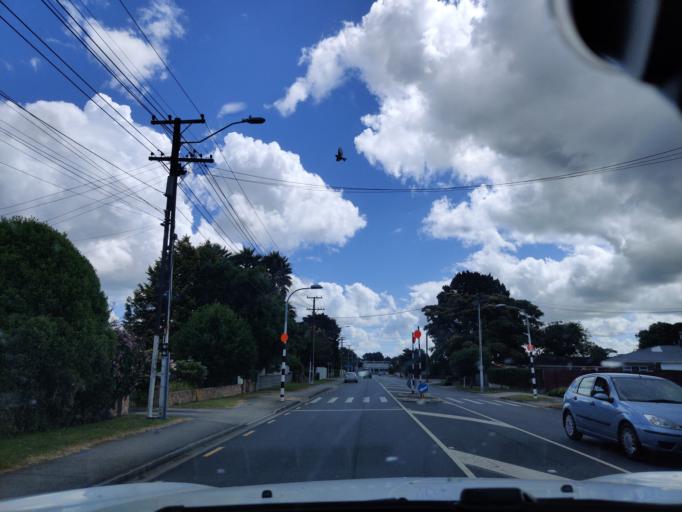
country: NZ
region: Auckland
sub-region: Auckland
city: Papakura
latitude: -37.0605
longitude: 174.9507
